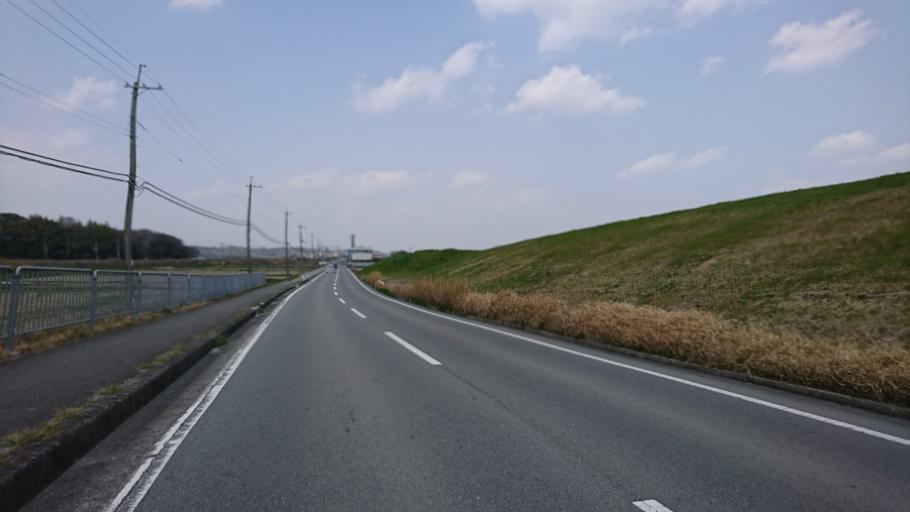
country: JP
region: Hyogo
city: Ono
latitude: 34.8469
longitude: 134.9101
